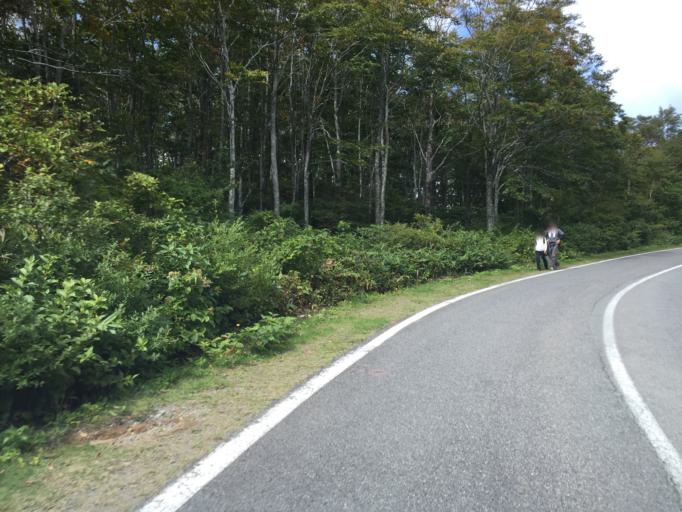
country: JP
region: Fukushima
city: Inawashiro
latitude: 37.6130
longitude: 140.0486
